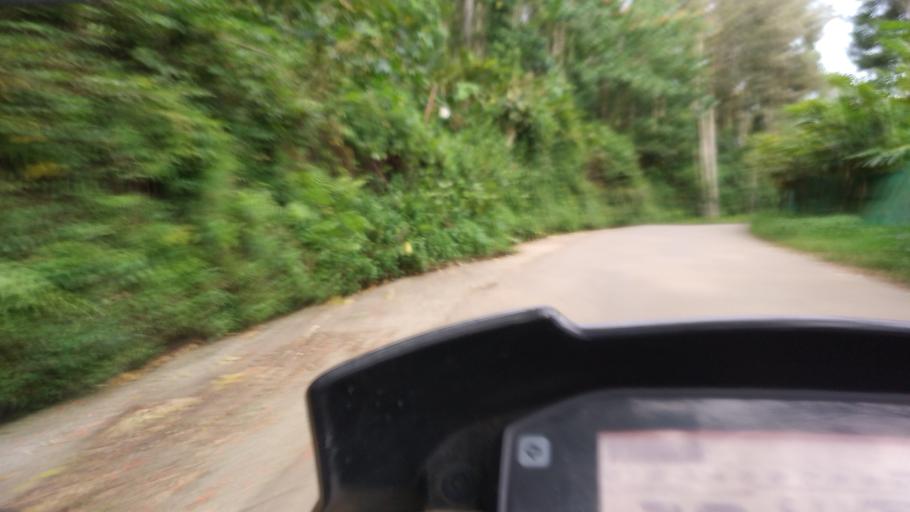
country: IN
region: Tamil Nadu
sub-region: Theni
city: Bodinayakkanur
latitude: 10.0246
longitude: 77.2367
